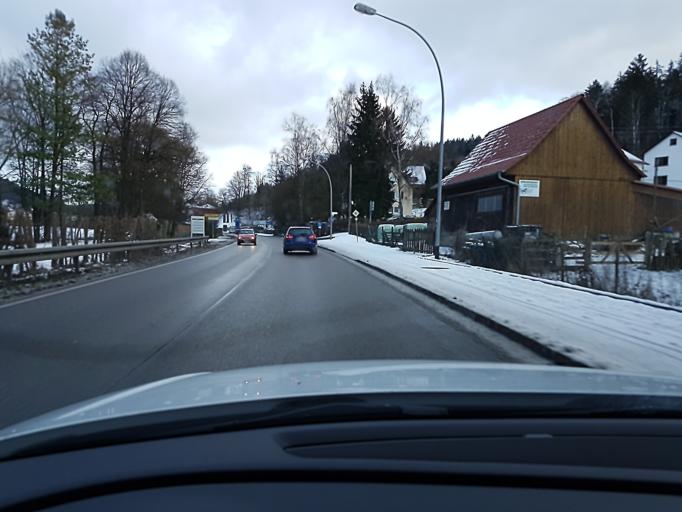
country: DE
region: Baden-Wuerttemberg
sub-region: Regierungsbezirk Stuttgart
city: Murrhardt
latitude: 48.9764
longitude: 9.5926
